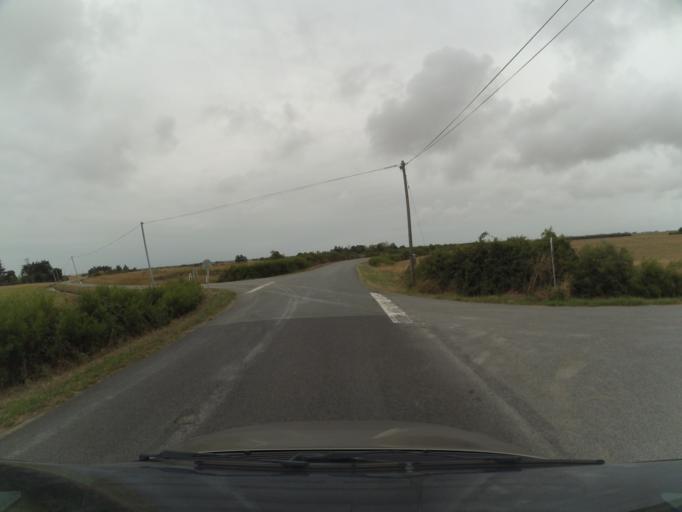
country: FR
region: Pays de la Loire
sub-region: Departement de la Vendee
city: Beauvoir-sur-Mer
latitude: 46.8789
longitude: -2.0740
